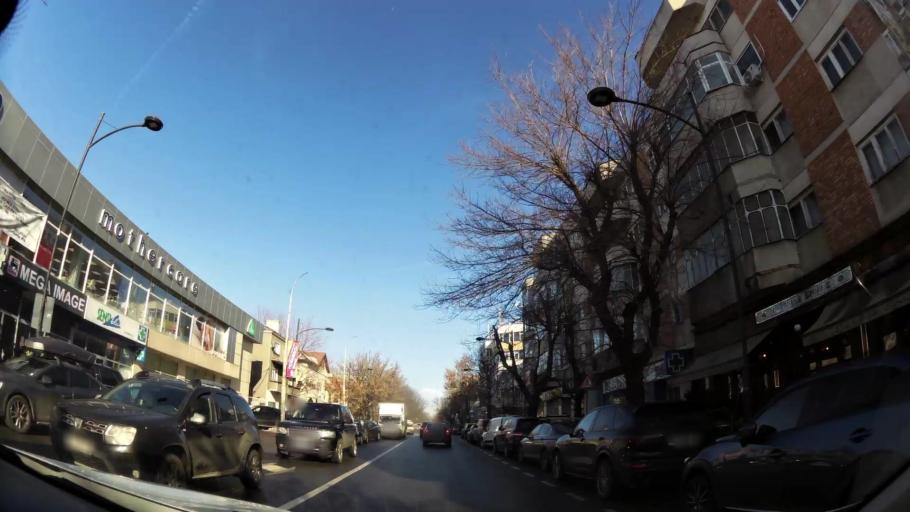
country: RO
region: Bucuresti
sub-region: Municipiul Bucuresti
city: Bucharest
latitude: 44.4610
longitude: 26.0946
